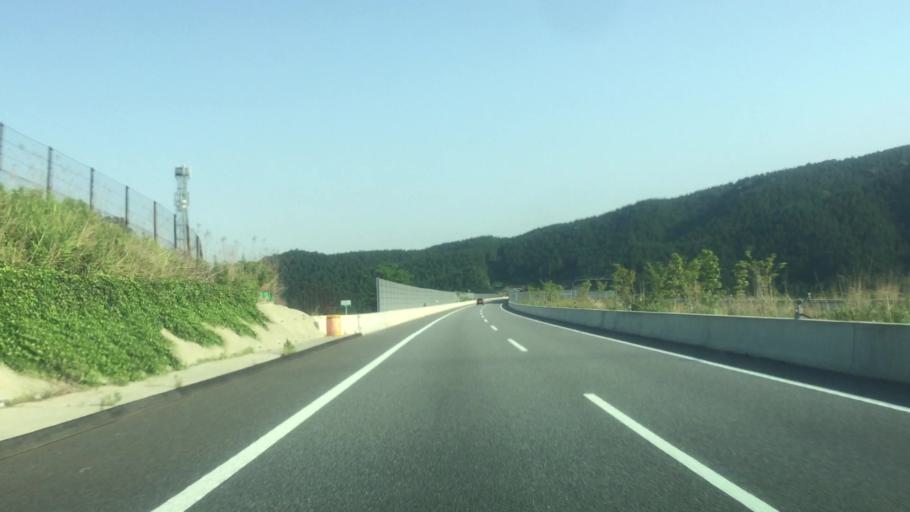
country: JP
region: Aichi
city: Okazaki
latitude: 34.9330
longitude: 137.2635
